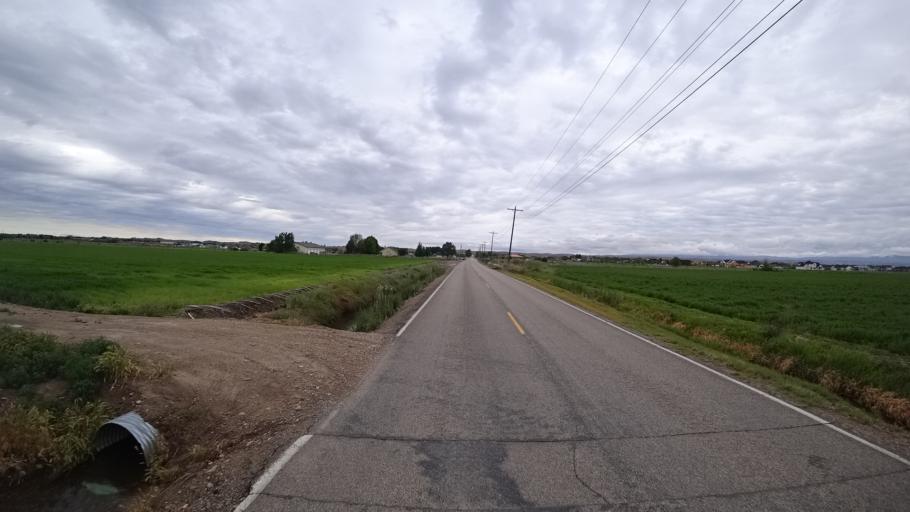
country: US
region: Idaho
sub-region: Ada County
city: Star
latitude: 43.6965
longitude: -116.4435
